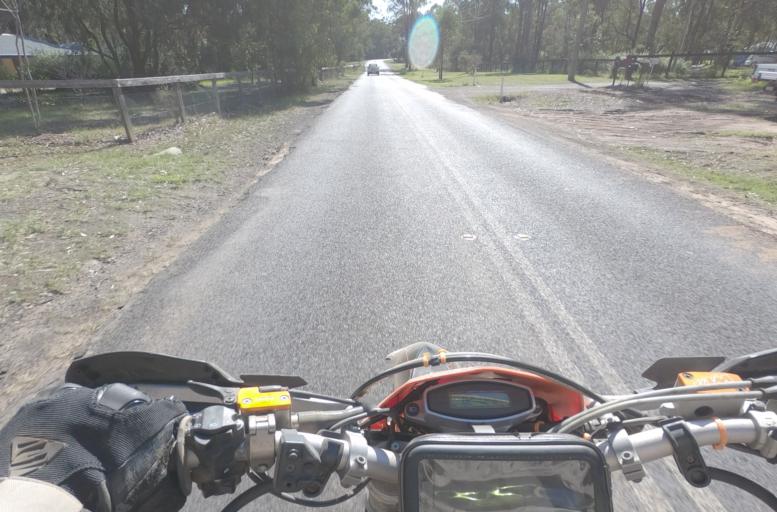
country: AU
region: New South Wales
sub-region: Hawkesbury
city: Pitt Town
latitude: -33.5818
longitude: 150.8793
